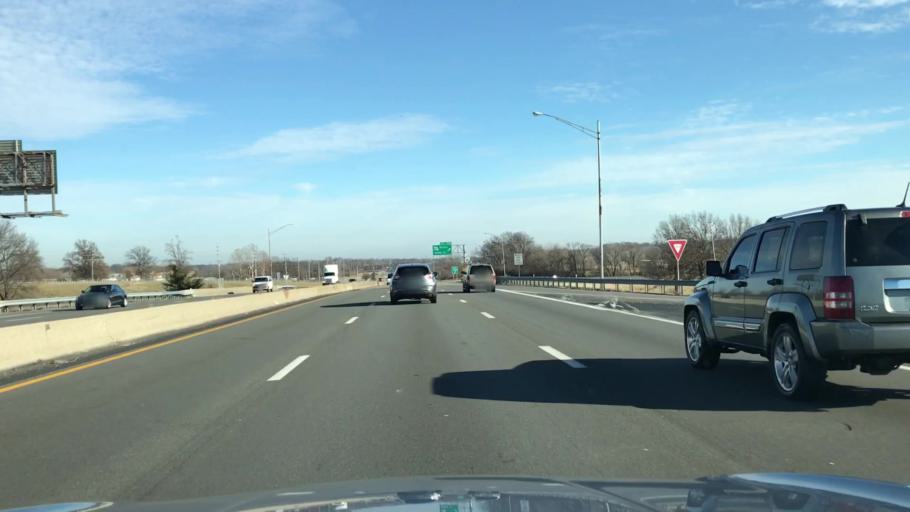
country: US
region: Missouri
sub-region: Saint Louis County
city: Castle Point
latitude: 38.7707
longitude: -90.2401
